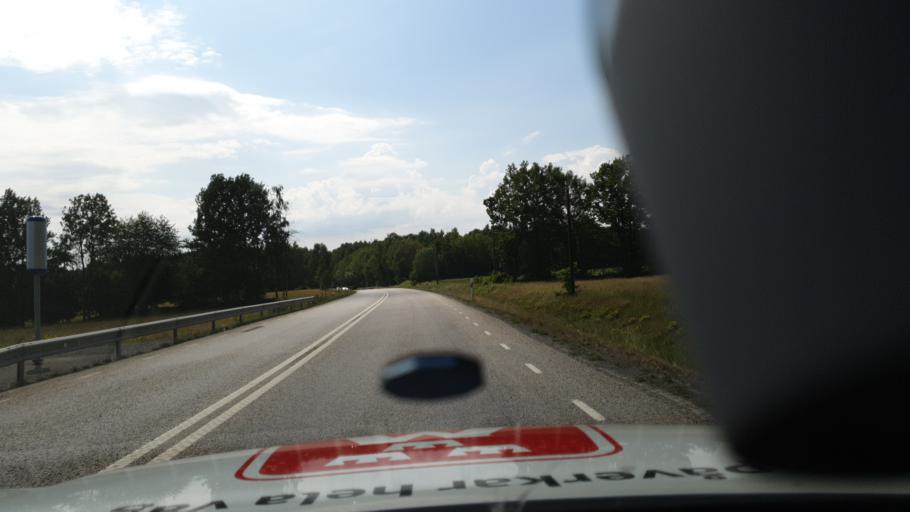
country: SE
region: Joenkoeping
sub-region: Habo Kommun
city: Habo
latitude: 57.9231
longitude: 14.0953
